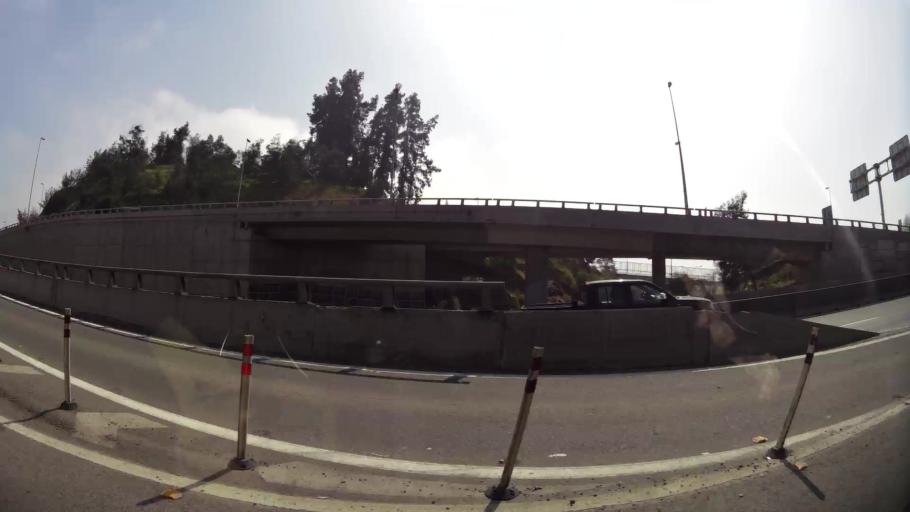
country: CL
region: Santiago Metropolitan
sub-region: Provincia de Santiago
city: Villa Presidente Frei, Nunoa, Santiago, Chile
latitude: -33.3898
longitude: -70.6005
